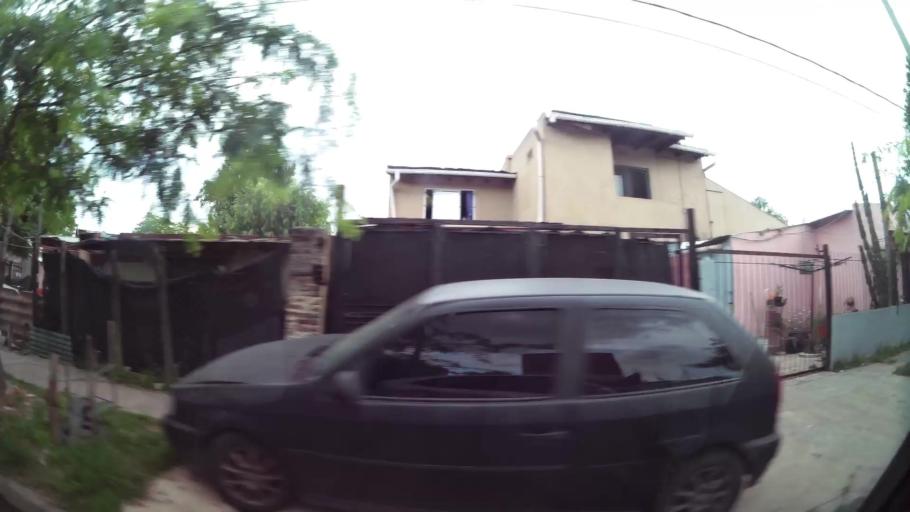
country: AR
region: Buenos Aires
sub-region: Partido de Tigre
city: Tigre
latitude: -34.4763
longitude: -58.6000
